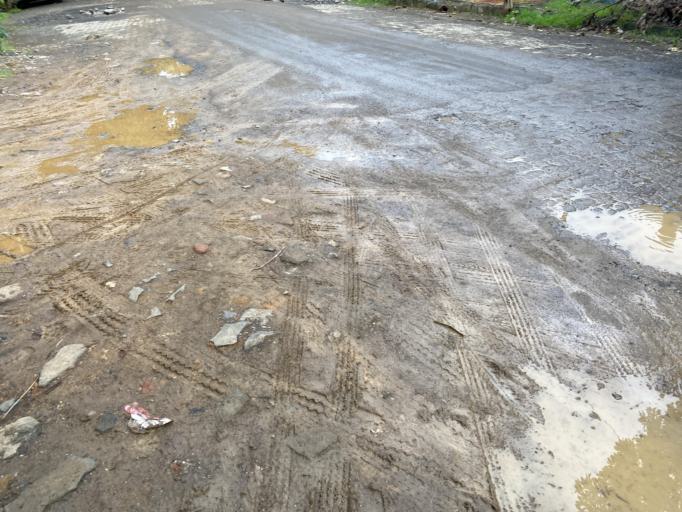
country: IN
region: Maharashtra
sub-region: Mumbai Suburban
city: Borivli
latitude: 19.2604
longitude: 72.8544
